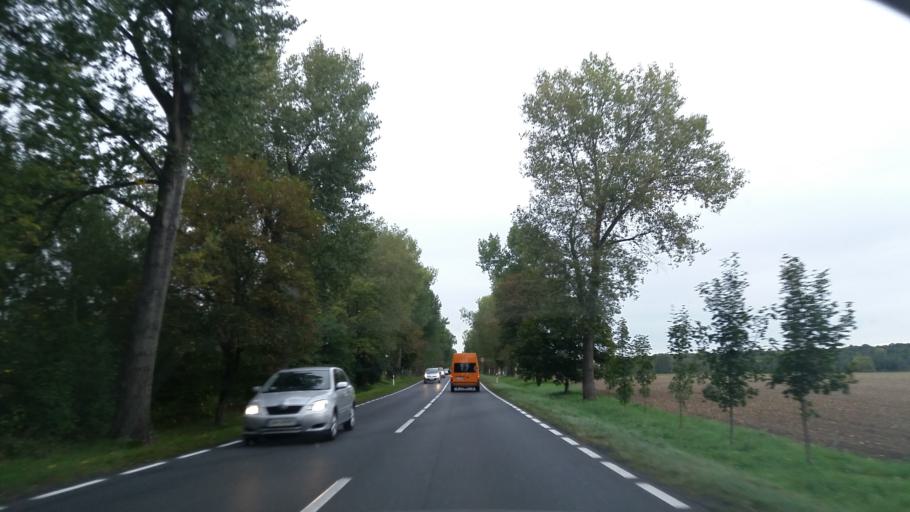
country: PL
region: Lower Silesian Voivodeship
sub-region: Powiat legnicki
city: Prochowice
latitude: 51.3085
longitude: 16.3306
